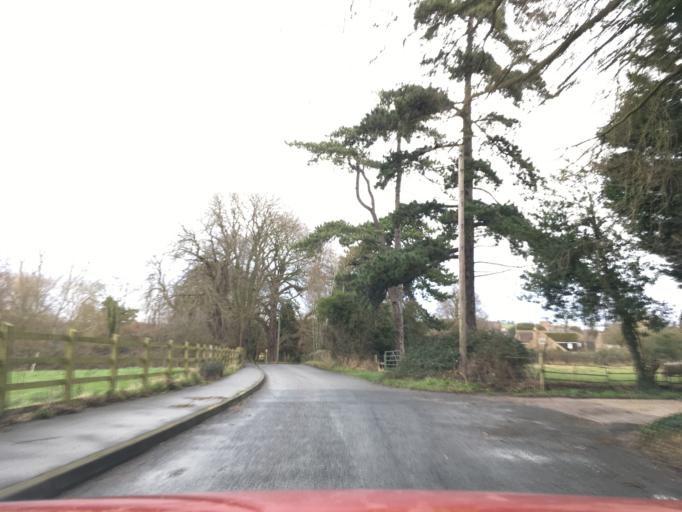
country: GB
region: England
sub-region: Gloucestershire
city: Gotherington
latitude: 52.0181
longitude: -2.0387
